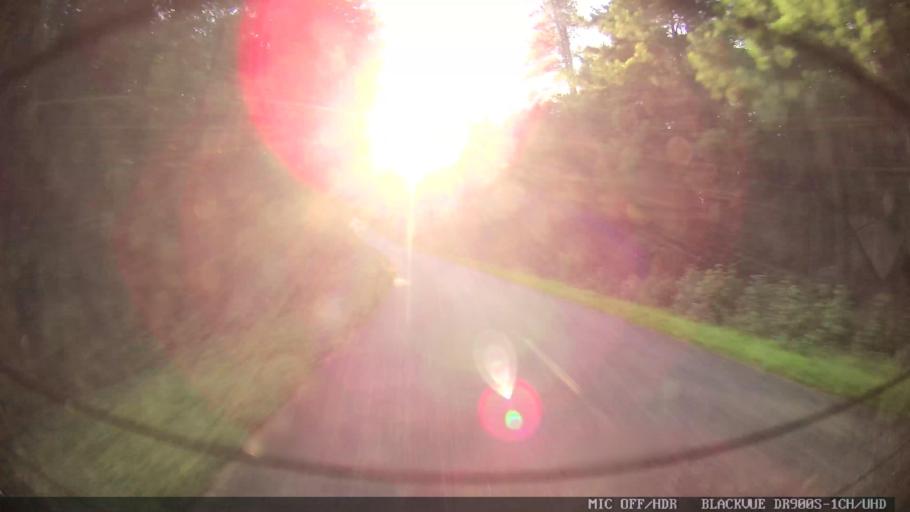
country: US
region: Georgia
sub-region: Bartow County
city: Emerson
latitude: 34.1872
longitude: -84.7021
